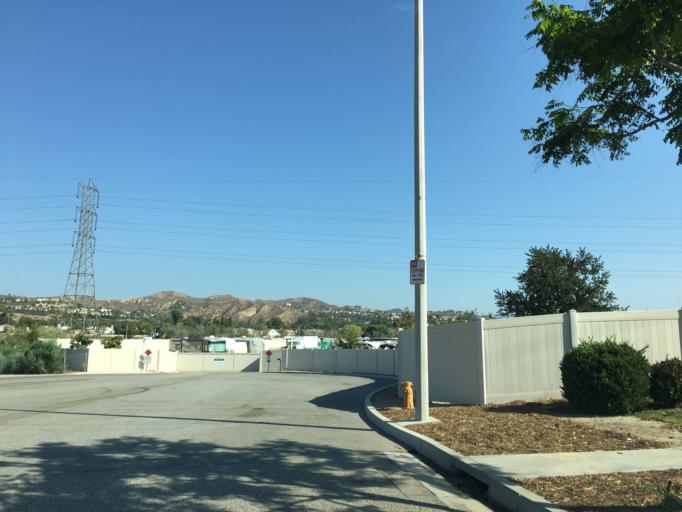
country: US
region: California
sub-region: Los Angeles County
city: Valencia
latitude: 34.4472
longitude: -118.6153
